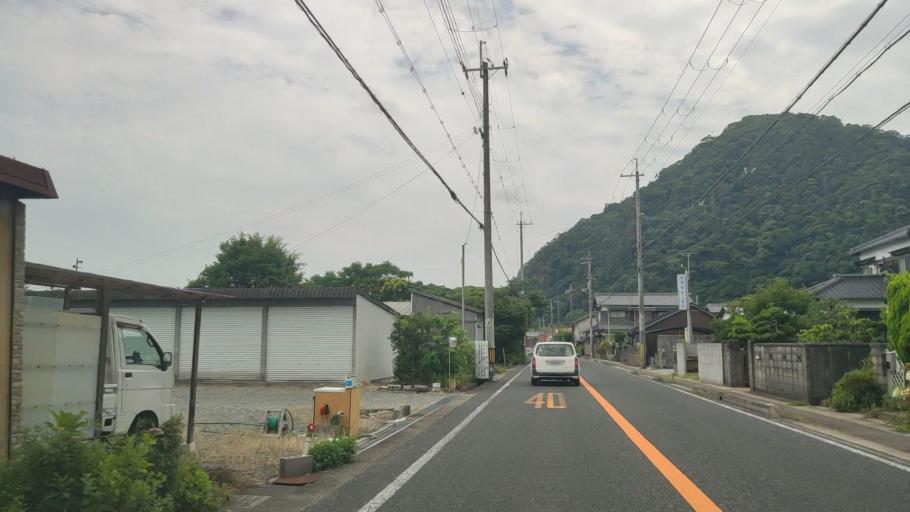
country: JP
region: Hyogo
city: Tatsunocho-tominaga
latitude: 34.8783
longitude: 134.5463
